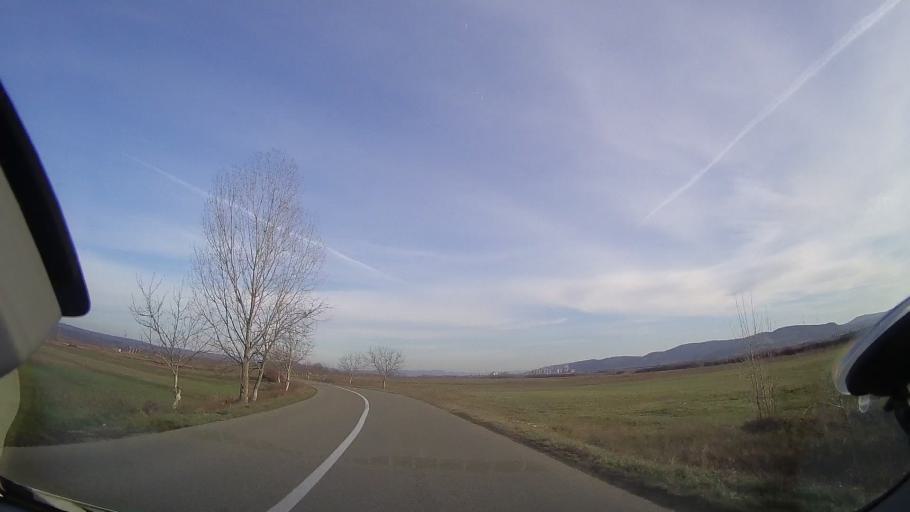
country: RO
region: Bihor
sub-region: Comuna Tetchea
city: Hotar
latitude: 47.0532
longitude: 22.2829
